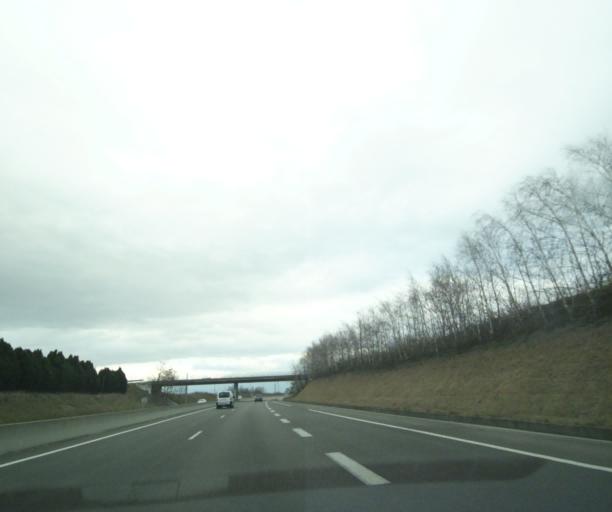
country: FR
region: Rhone-Alpes
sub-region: Departement de la Drome
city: Bourg-les-Valence
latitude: 44.9649
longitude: 4.9145
